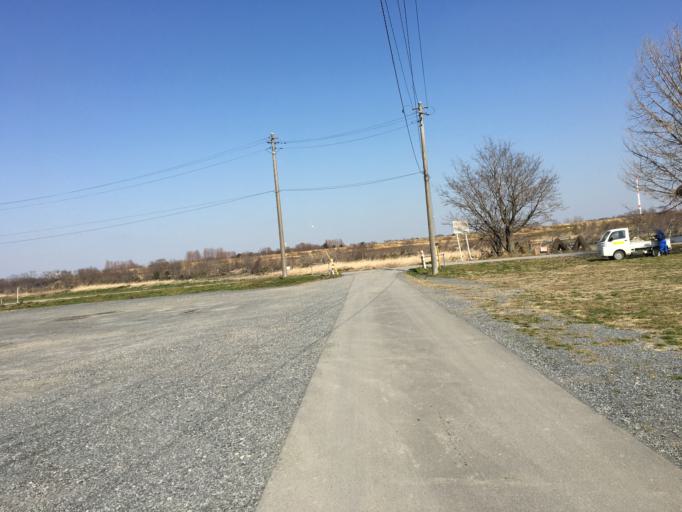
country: JP
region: Saitama
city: Shiki
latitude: 35.8454
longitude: 139.5973
